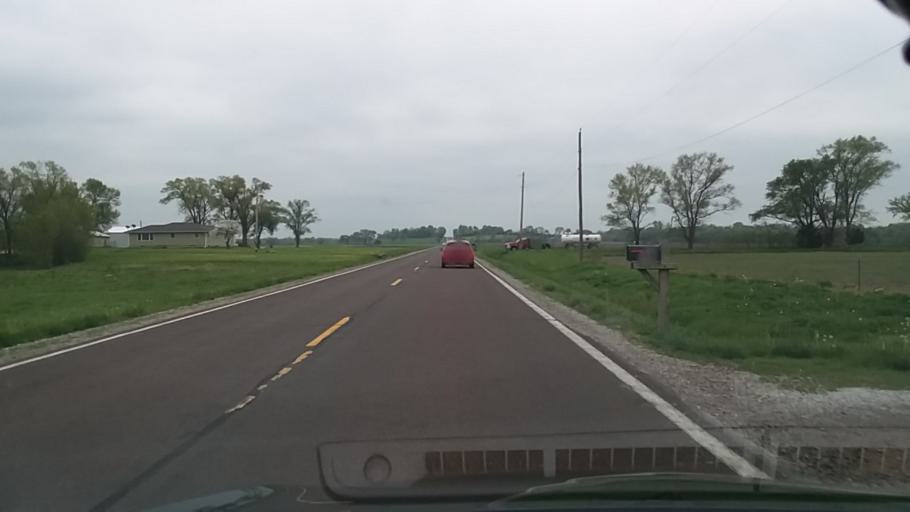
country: US
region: Kansas
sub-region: Douglas County
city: Eudora
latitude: 38.8524
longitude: -95.0932
